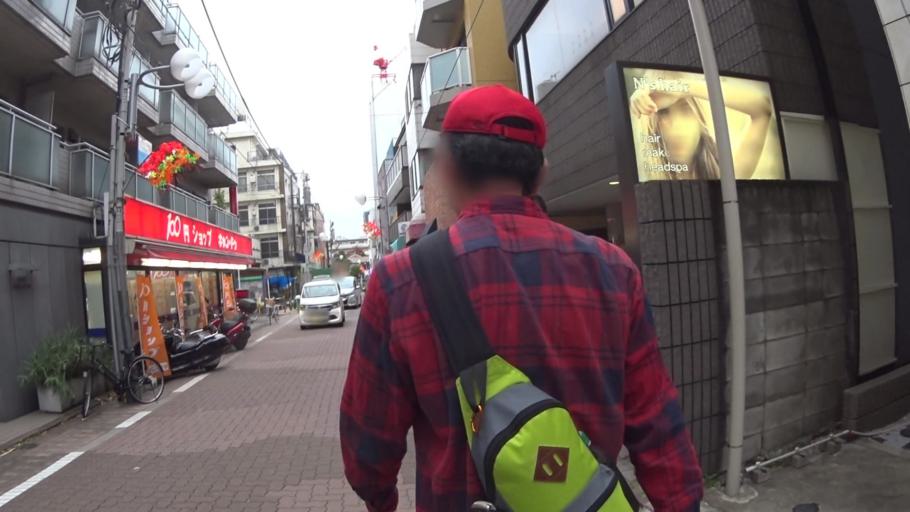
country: JP
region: Tokyo
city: Tokyo
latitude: 35.6438
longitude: 139.7314
